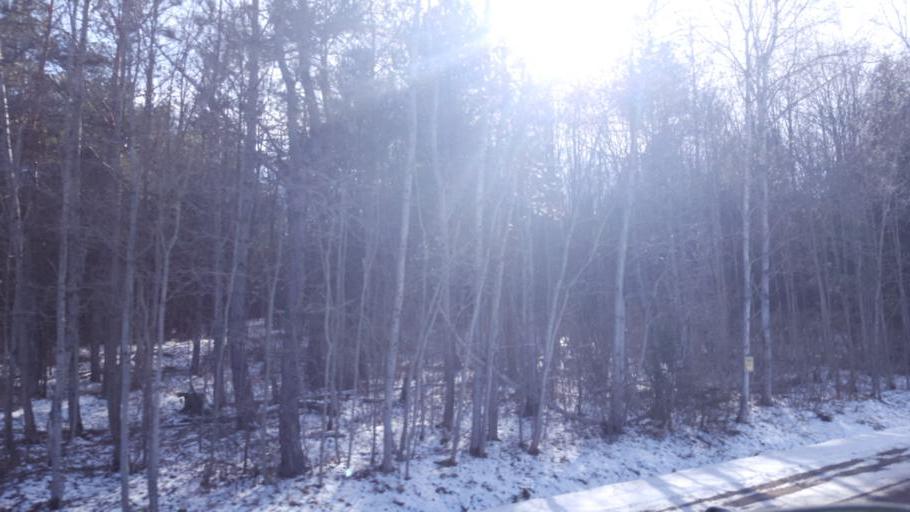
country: US
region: New York
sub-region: Allegany County
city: Wellsville
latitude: 42.1221
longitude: -77.9866
